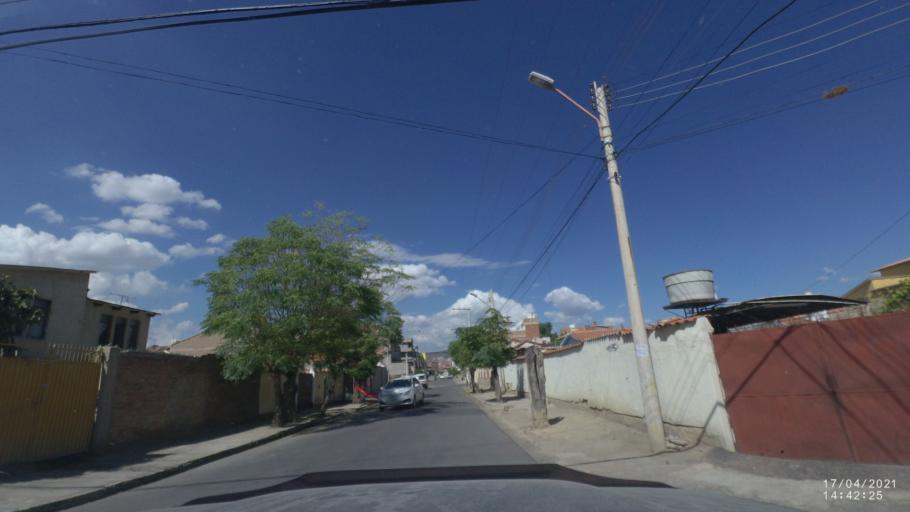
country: BO
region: Cochabamba
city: Cochabamba
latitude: -17.4126
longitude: -66.1669
